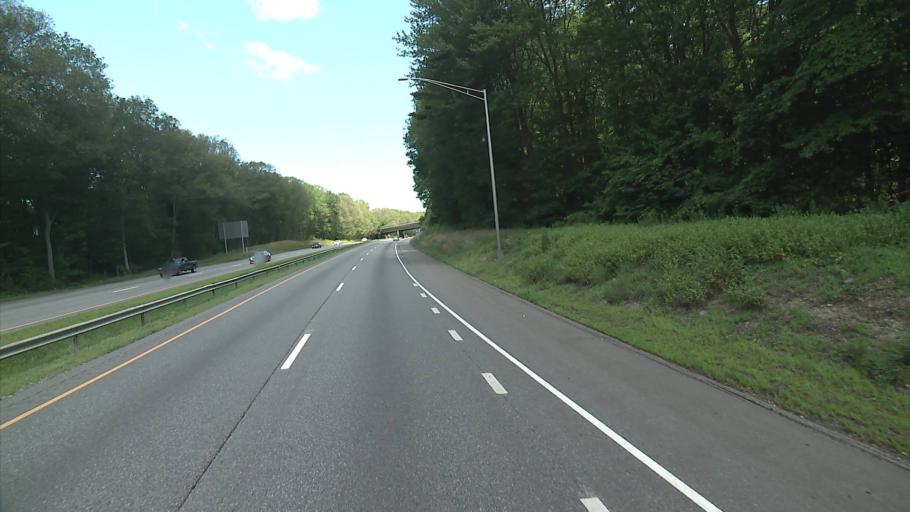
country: US
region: Connecticut
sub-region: New London County
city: Norwich
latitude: 41.5150
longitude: -72.1191
